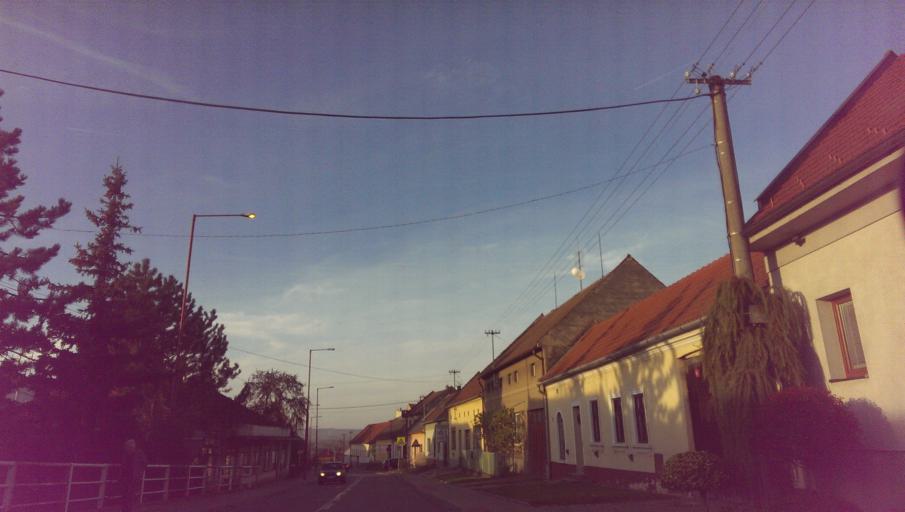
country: CZ
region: Zlin
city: Kunovice
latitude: 49.0639
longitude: 17.4814
